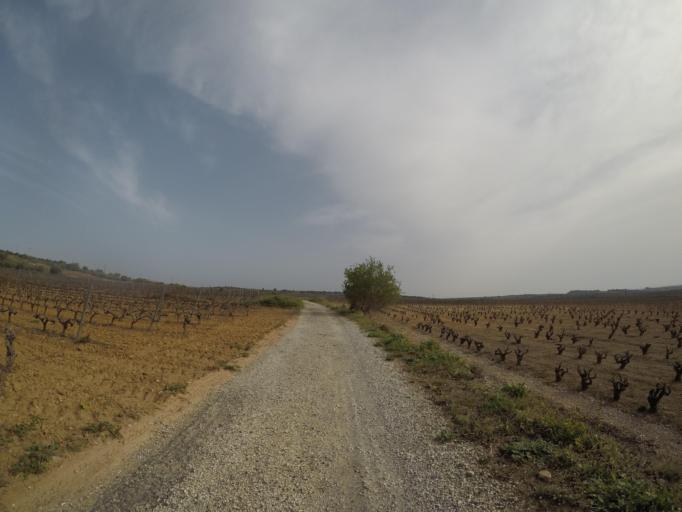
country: FR
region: Languedoc-Roussillon
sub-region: Departement des Pyrenees-Orientales
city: Baixas
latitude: 42.7589
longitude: 2.8176
